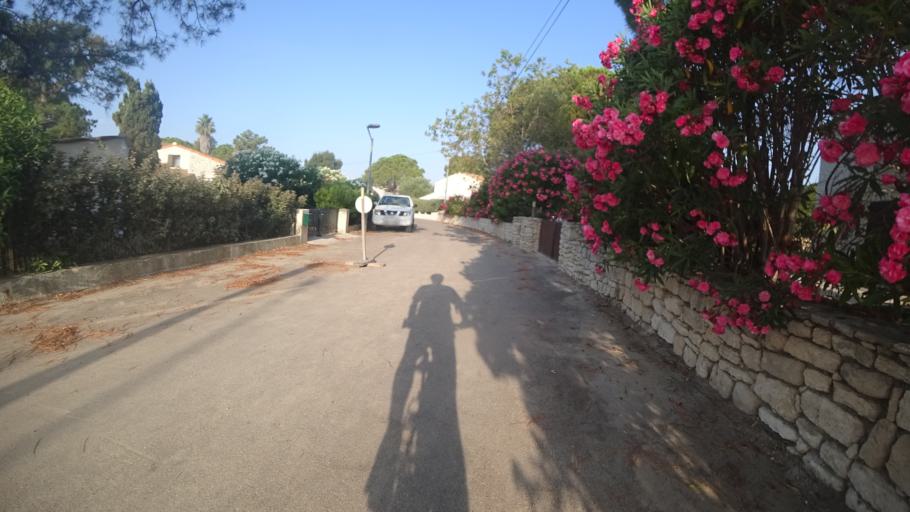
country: FR
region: Corsica
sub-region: Departement de la Corse-du-Sud
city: Porto-Vecchio
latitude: 41.6341
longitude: 9.3463
